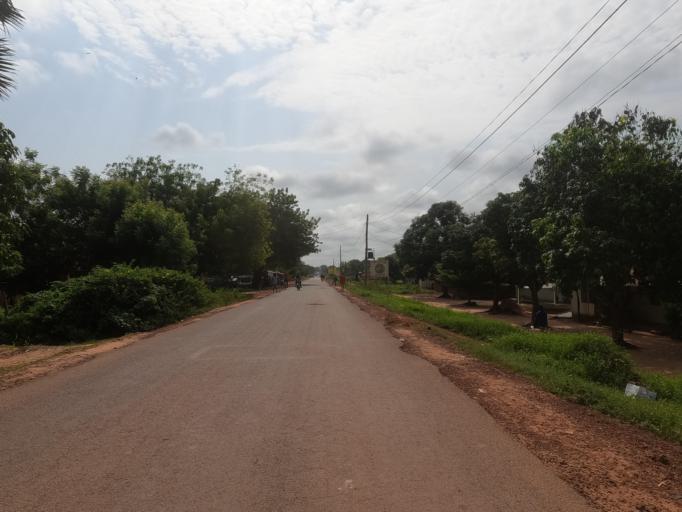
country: SN
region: Ziguinchor
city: Adeane
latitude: 12.4023
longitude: -15.7926
